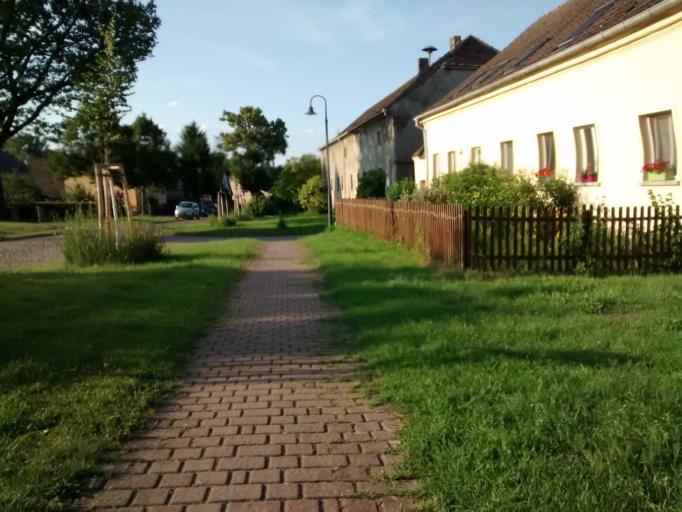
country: DE
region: Brandenburg
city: Hohen Neuendorf
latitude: 52.6619
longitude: 13.2603
